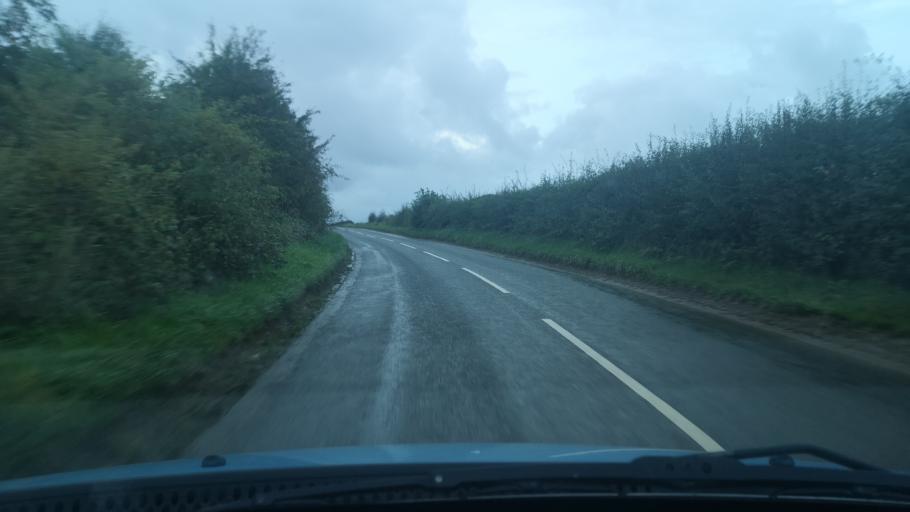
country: GB
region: England
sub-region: Doncaster
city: Norton
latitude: 53.6383
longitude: -1.2095
